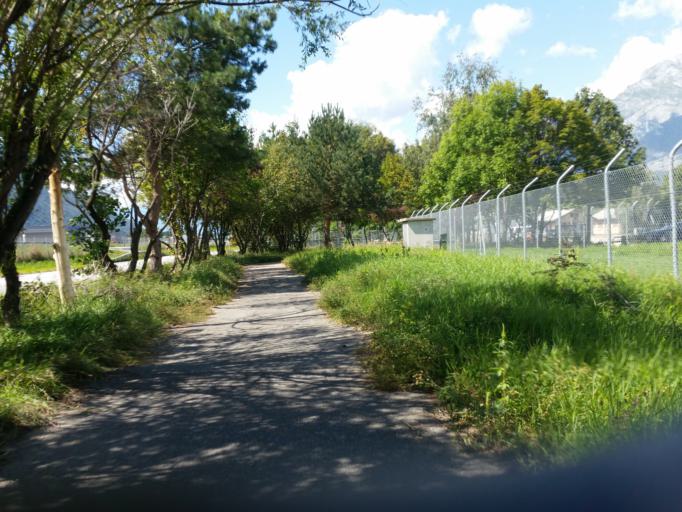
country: CH
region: Valais
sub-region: Sion District
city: Sitten
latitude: 46.2206
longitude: 7.3439
